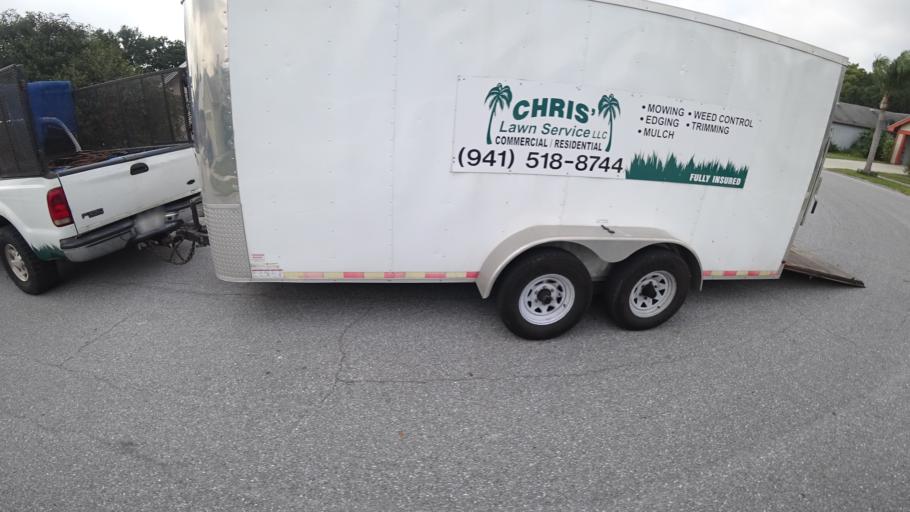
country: US
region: Florida
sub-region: Sarasota County
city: North Sarasota
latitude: 27.4068
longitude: -82.5146
